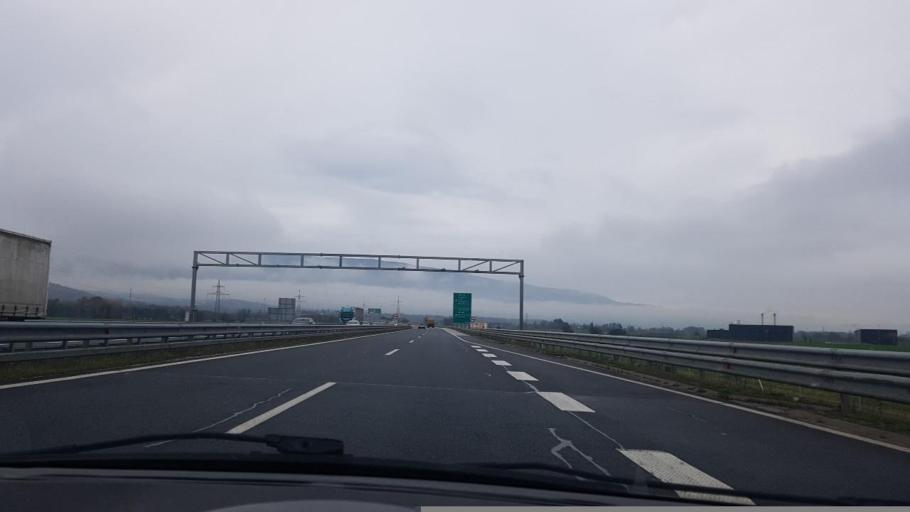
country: SI
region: Hoce-Slivnica
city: Hotinja Vas
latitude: 46.4750
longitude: 15.6725
